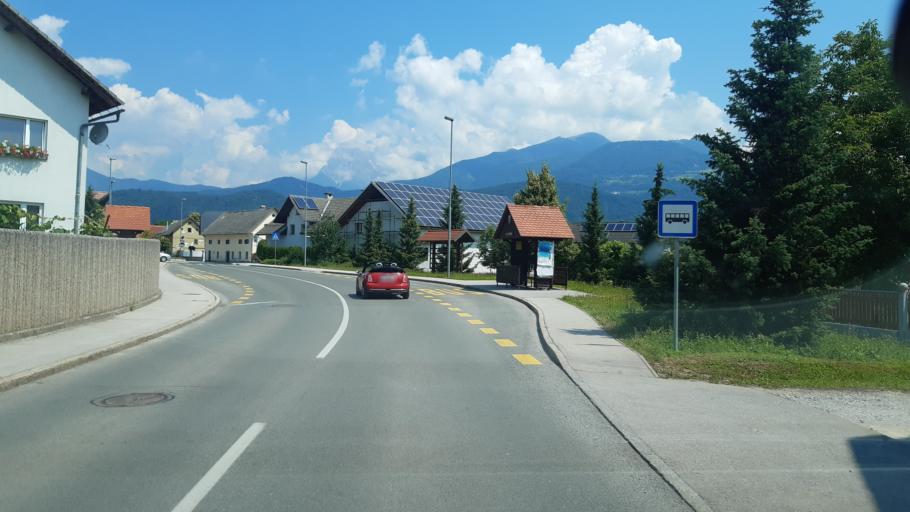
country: SI
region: Cerklje na Gorenjskem
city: Cerklje na Gorenjskem
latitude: 46.2384
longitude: 14.4848
